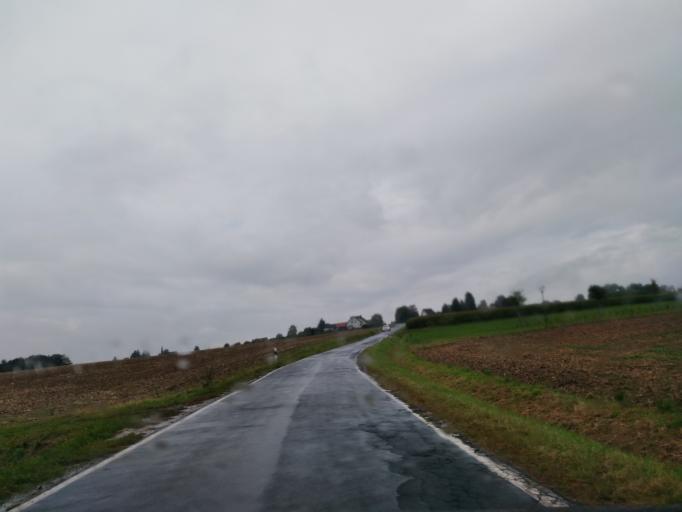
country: DE
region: Rheinland-Pfalz
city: Kircheib
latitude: 50.6798
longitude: 7.4502
